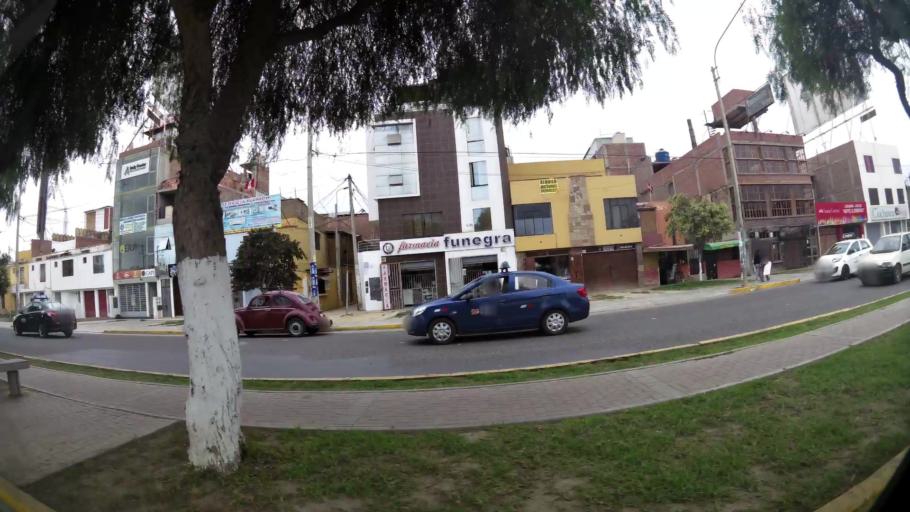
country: PE
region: La Libertad
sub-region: Provincia de Trujillo
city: Trujillo
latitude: -8.1260
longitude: -79.0351
